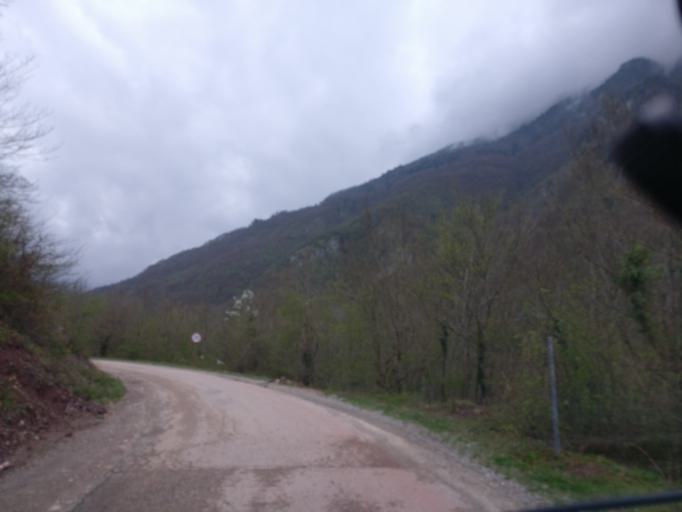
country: BA
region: Republika Srpska
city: Foca
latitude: 43.3553
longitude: 18.8176
